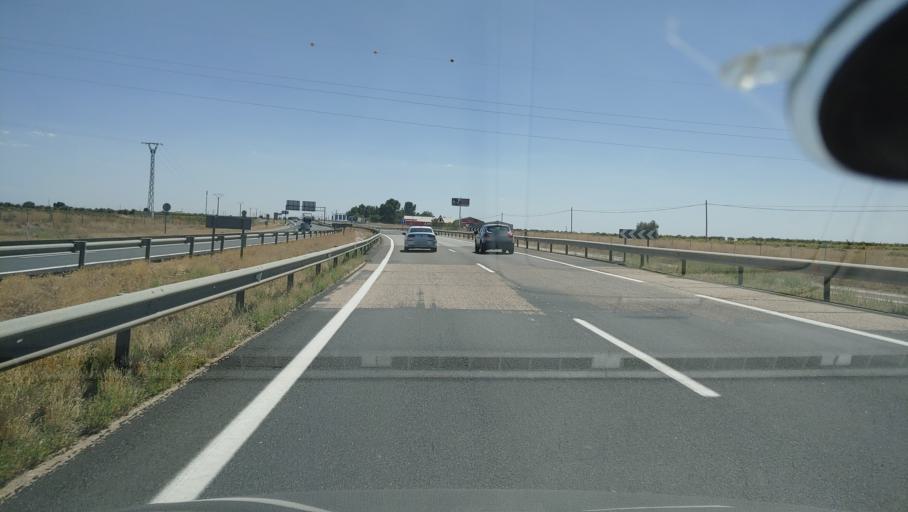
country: ES
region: Castille-La Mancha
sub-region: Provincia de Ciudad Real
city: Villarta de San Juan
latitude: 39.2195
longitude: -3.4137
